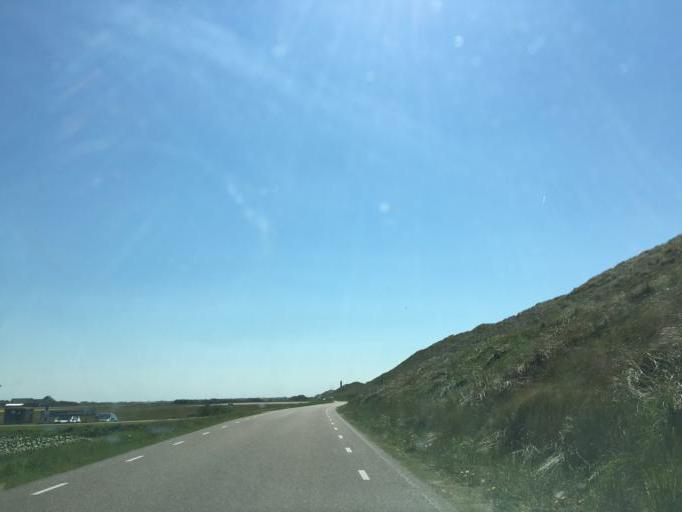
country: NL
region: North Holland
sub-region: Gemeente Den Helder
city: Den Helder
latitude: 52.8903
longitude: 4.7169
